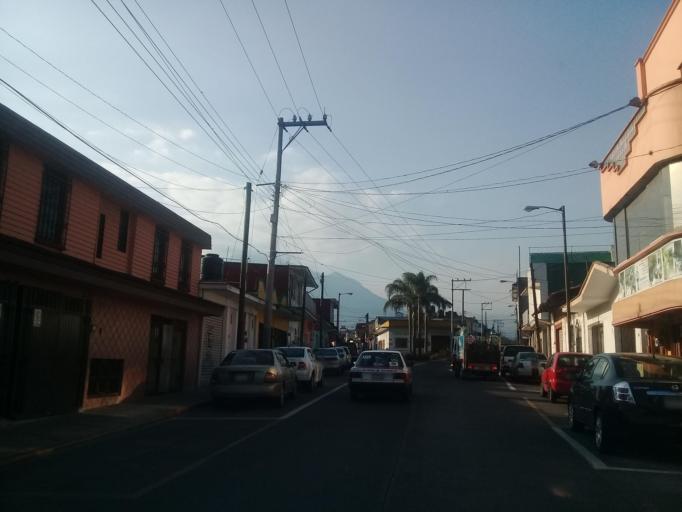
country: MX
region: Veracruz
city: Orizaba
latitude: 18.8540
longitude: -97.1096
